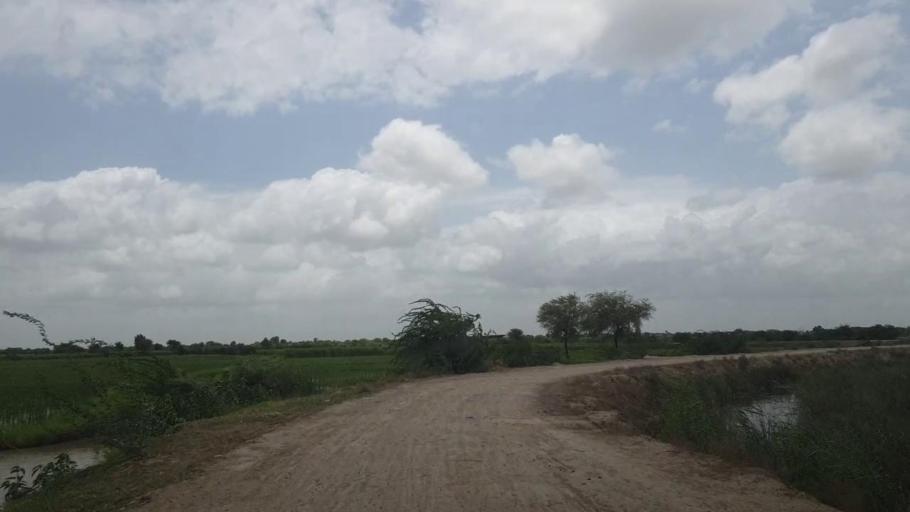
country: PK
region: Sindh
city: Badin
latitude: 24.6535
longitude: 68.9212
